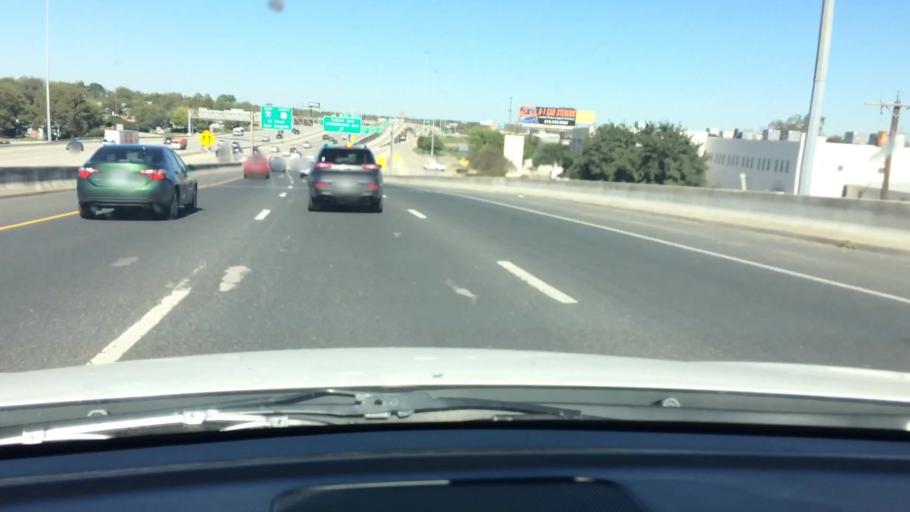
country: US
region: Texas
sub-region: Bexar County
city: Olmos Park
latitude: 29.4572
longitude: -98.5153
